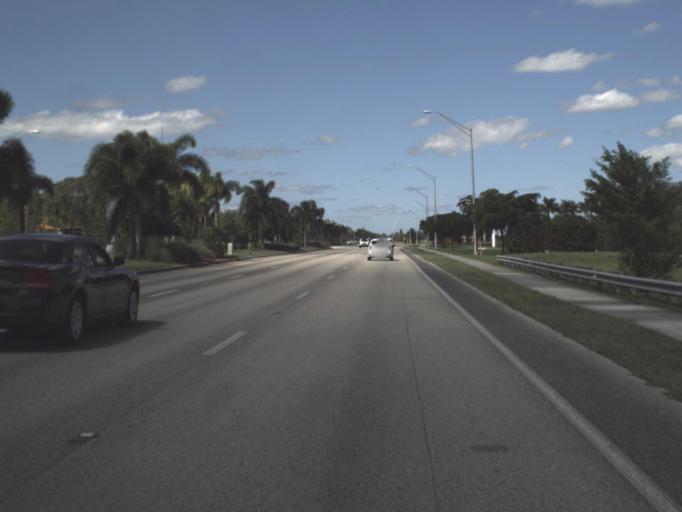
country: US
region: Florida
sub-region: Collier County
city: Lely Resort
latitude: 26.0668
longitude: -81.7044
